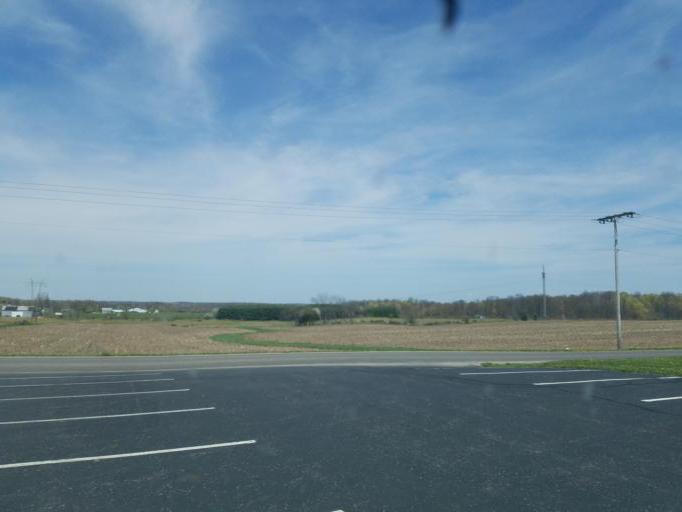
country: US
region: Ohio
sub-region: Richland County
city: Lexington
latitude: 40.5865
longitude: -82.6610
